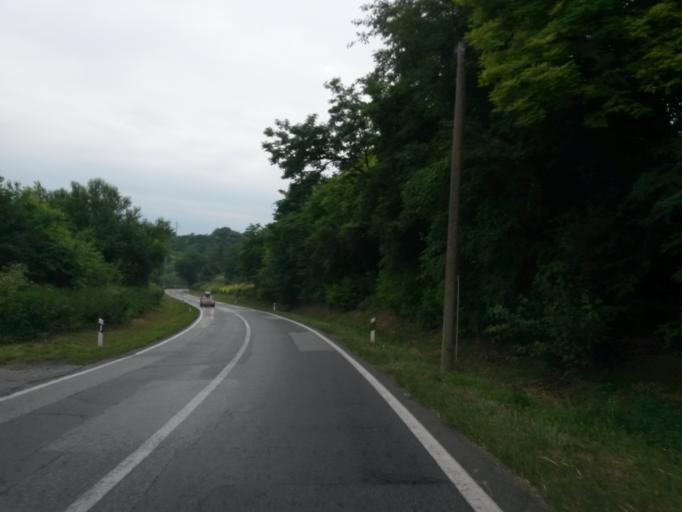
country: HR
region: Vukovarsko-Srijemska
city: Ilok
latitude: 45.2239
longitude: 19.3433
